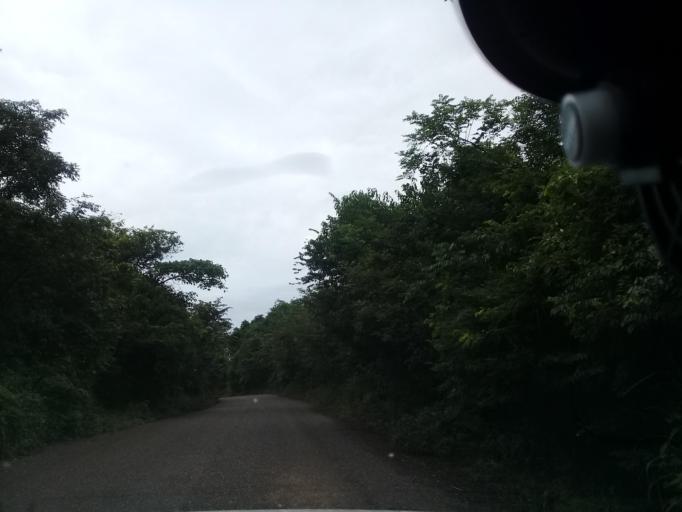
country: MX
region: Hidalgo
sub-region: Huejutla de Reyes
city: Chalahuiyapa
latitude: 21.2112
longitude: -98.3600
